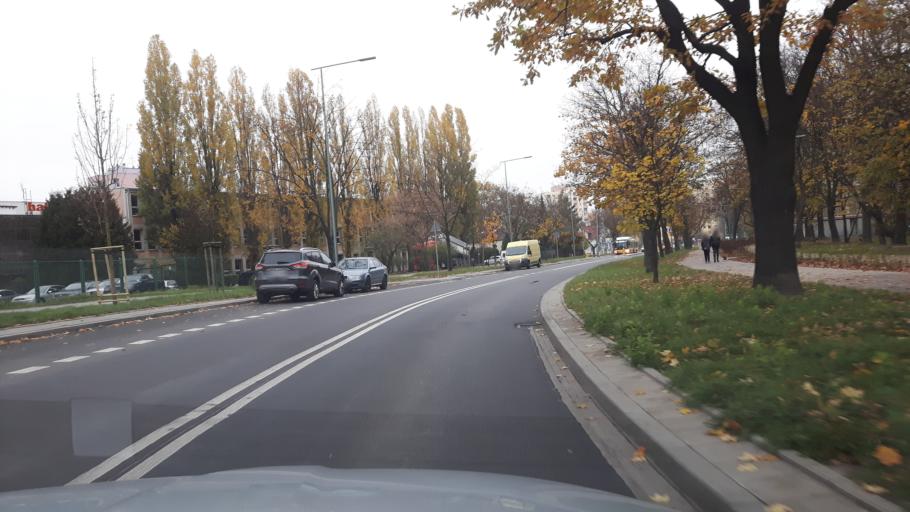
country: PL
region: Masovian Voivodeship
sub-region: Warszawa
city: Praga Polnoc
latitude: 52.2712
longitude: 21.0459
